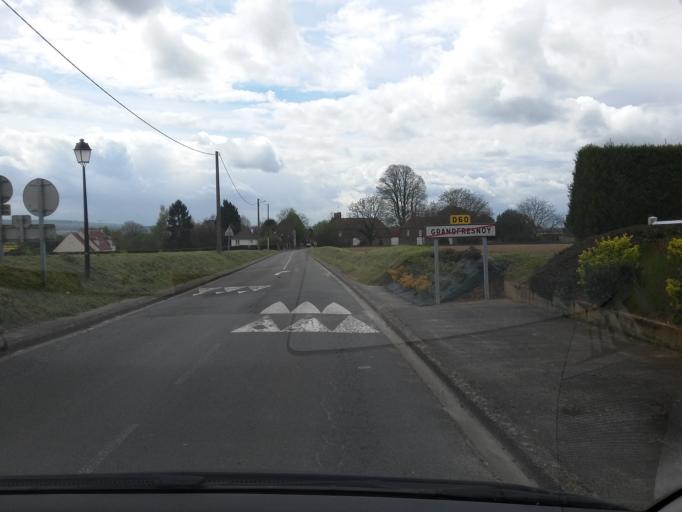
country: FR
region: Picardie
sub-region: Departement de l'Oise
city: Grandfresnoy
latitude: 49.3667
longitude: 2.6447
